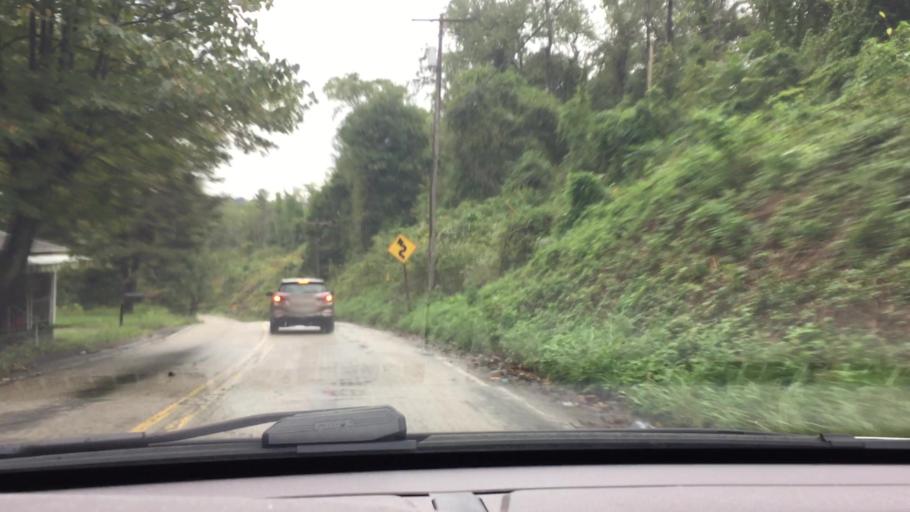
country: US
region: Pennsylvania
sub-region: Westmoreland County
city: North Belle Vernon
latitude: 40.1355
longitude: -79.8749
